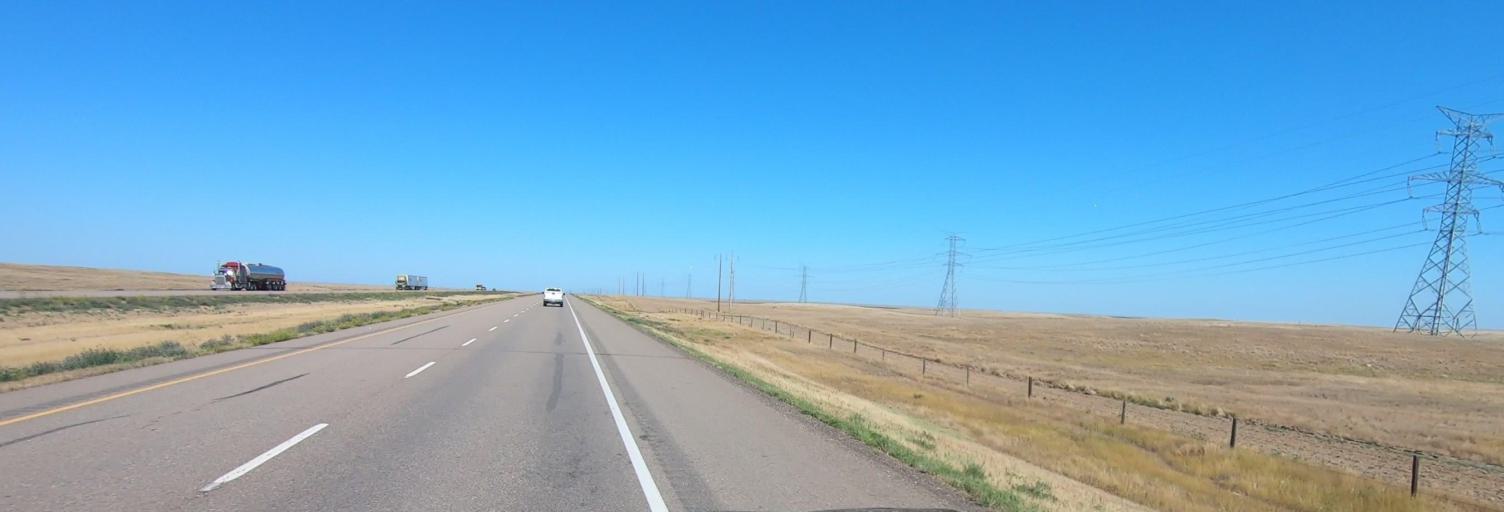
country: CA
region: Alberta
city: Bow Island
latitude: 50.3187
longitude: -111.3468
